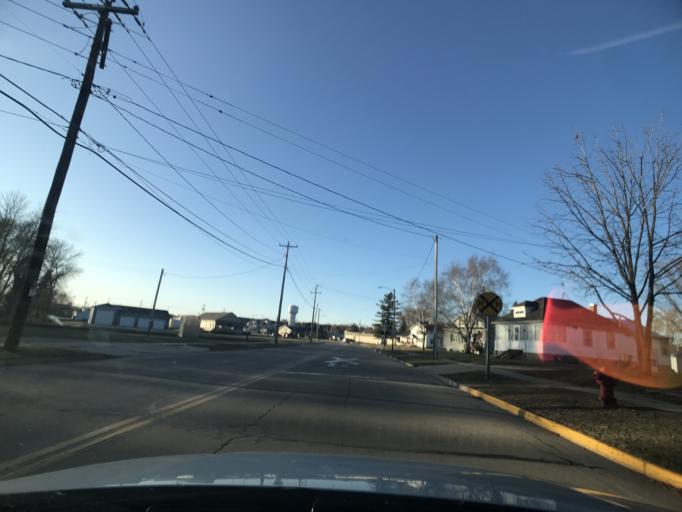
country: US
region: Wisconsin
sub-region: Oconto County
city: Oconto
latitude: 44.8925
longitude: -87.8813
